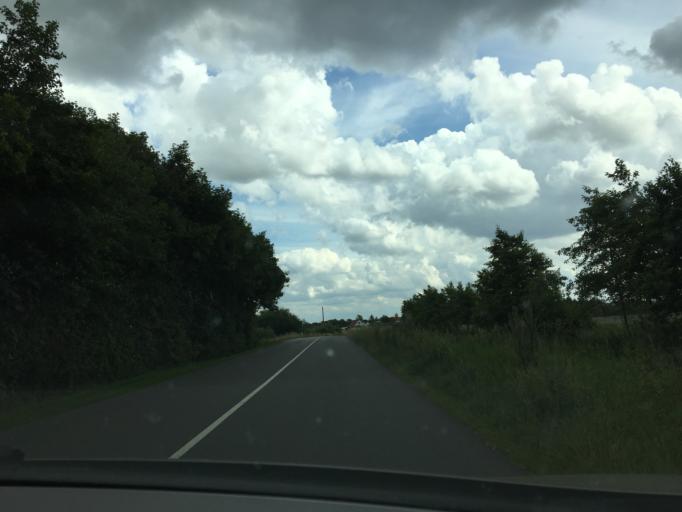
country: DK
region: Central Jutland
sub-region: Ringkobing-Skjern Kommune
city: Skjern
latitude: 55.9494
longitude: 8.4714
